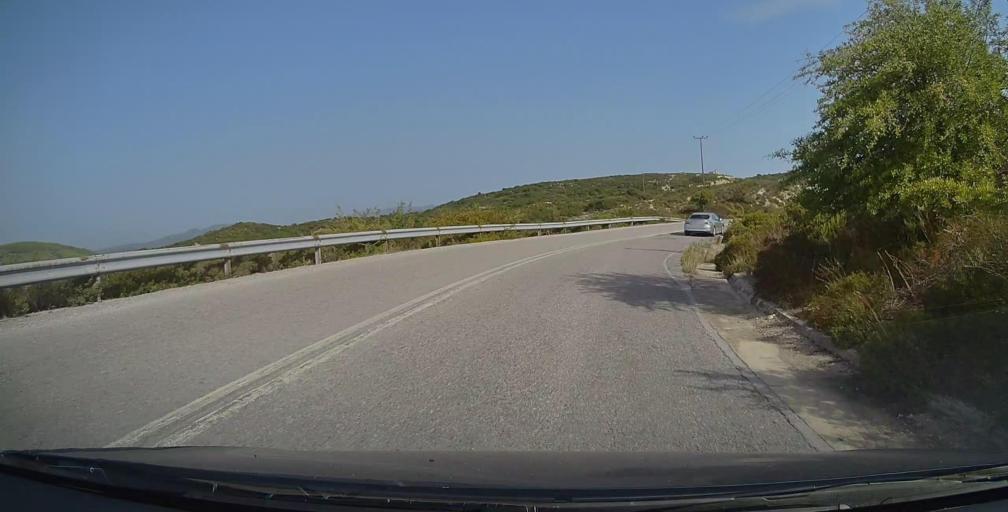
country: GR
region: Central Macedonia
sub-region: Nomos Chalkidikis
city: Sykia
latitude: 39.9759
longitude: 23.9591
